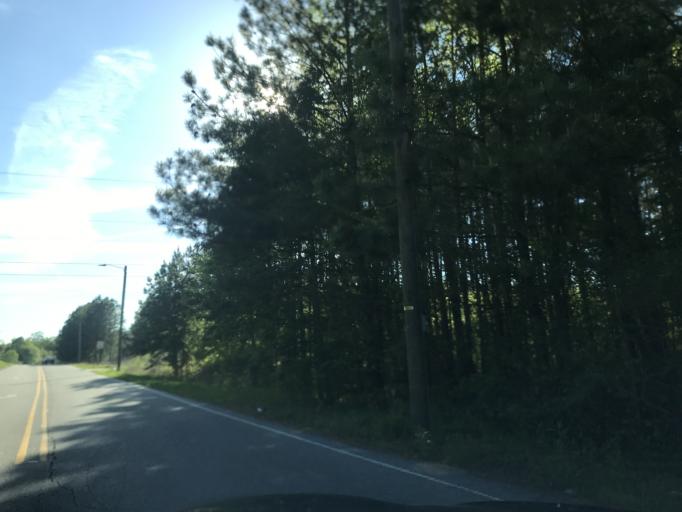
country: US
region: North Carolina
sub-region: Wake County
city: Knightdale
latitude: 35.8130
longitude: -78.5567
